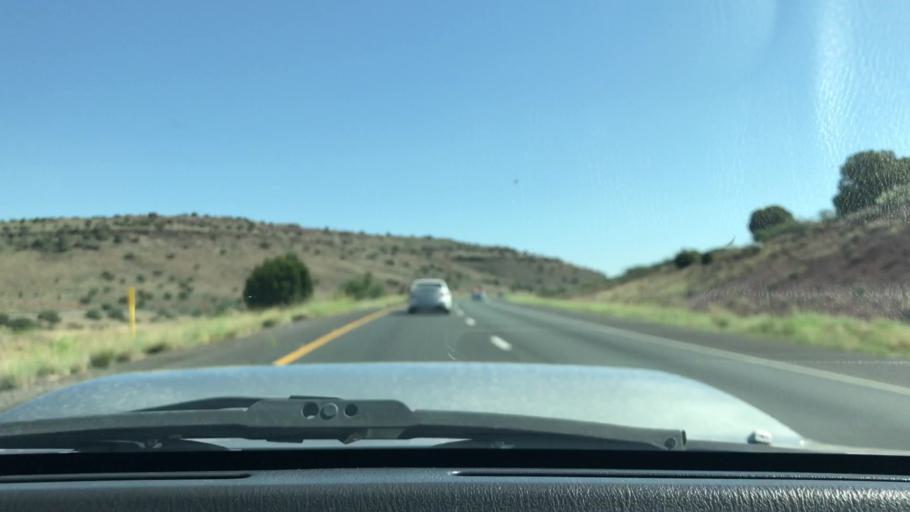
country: US
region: Arizona
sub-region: Yavapai County
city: Camp Verde
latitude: 34.4786
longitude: -112.0201
